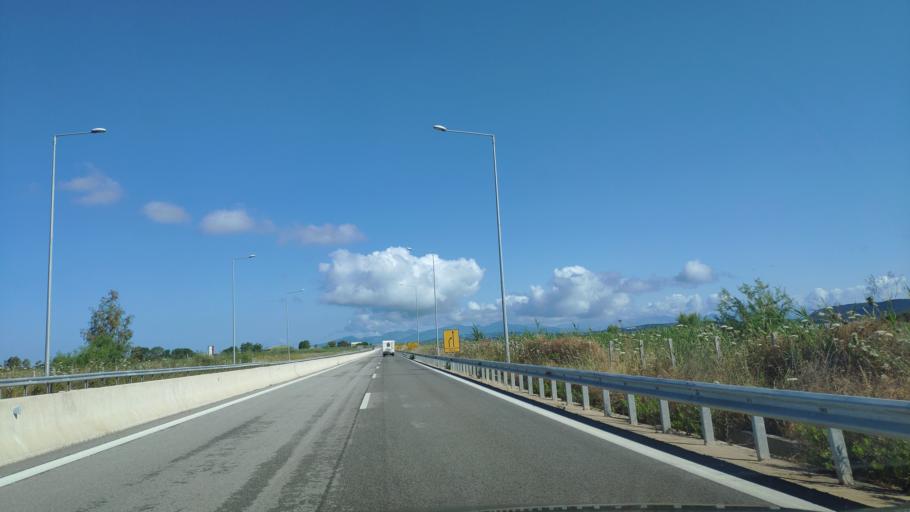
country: GR
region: Epirus
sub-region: Nomos Prevezis
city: Preveza
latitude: 38.9197
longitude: 20.7894
